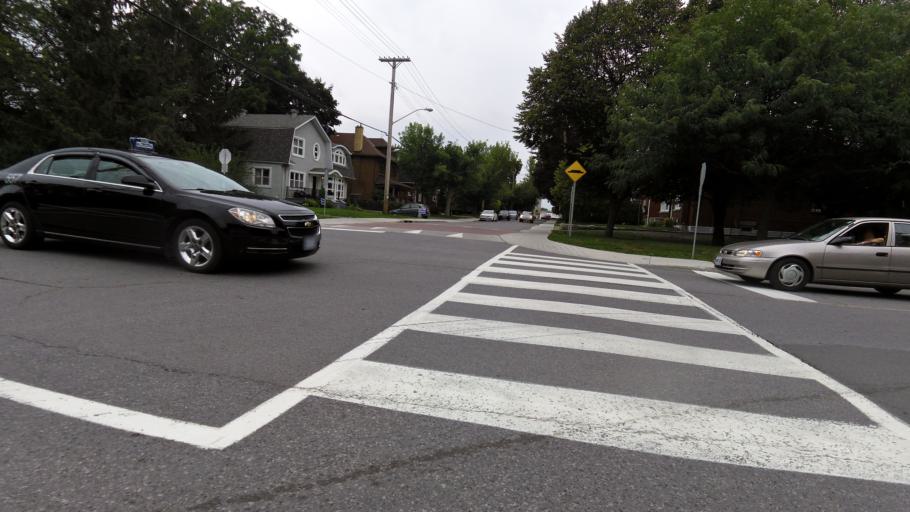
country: CA
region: Ontario
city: Ottawa
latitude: 45.3973
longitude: -75.7327
